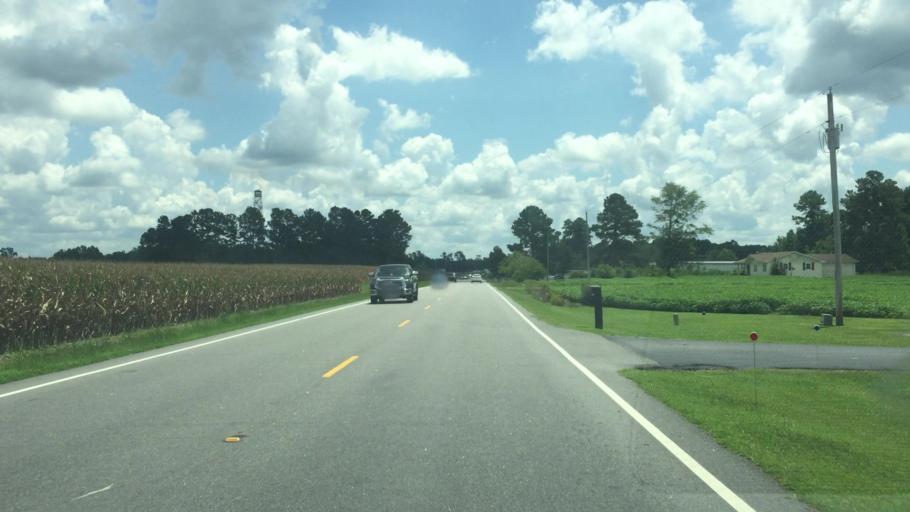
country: US
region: North Carolina
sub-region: Columbus County
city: Chadbourn
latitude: 34.2815
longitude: -78.8178
